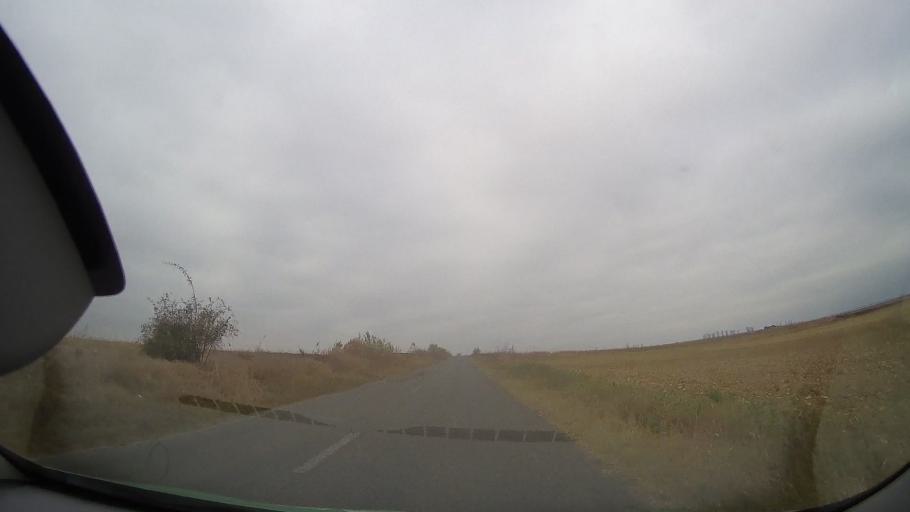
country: RO
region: Buzau
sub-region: Comuna Luciu
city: Luciu
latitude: 44.9776
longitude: 27.0542
